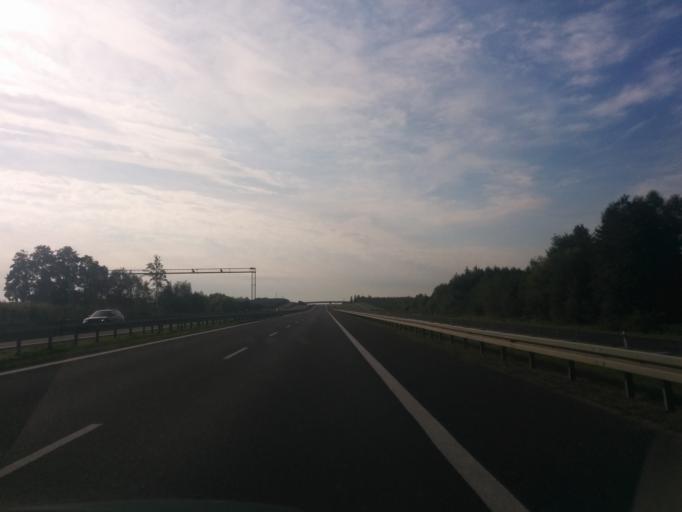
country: PL
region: Masovian Voivodeship
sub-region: Powiat grojecki
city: Jasieniec
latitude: 51.7962
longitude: 20.8904
